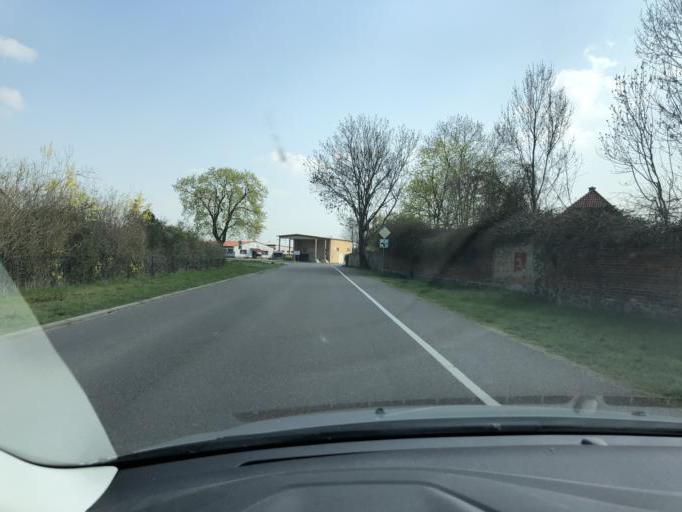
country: DE
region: Saxony-Anhalt
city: Niemberg
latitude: 51.5979
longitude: 12.0668
